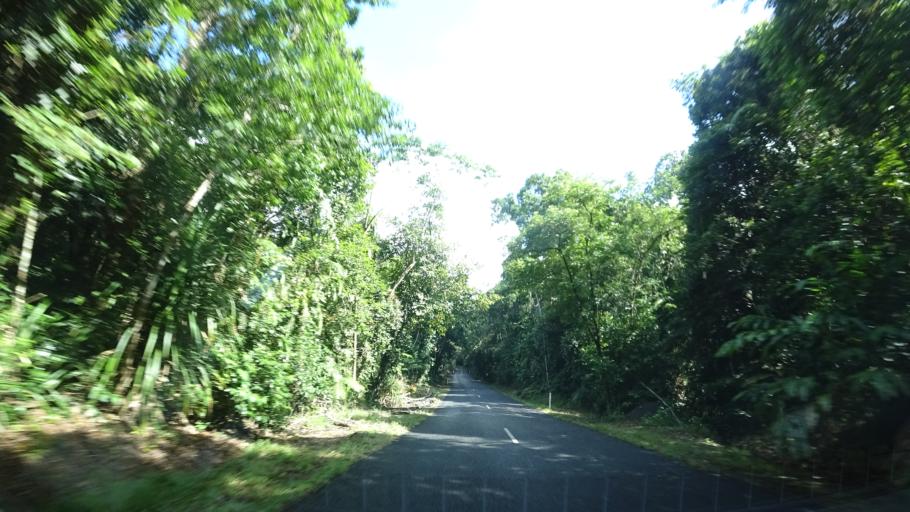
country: AU
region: Queensland
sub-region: Cairns
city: Port Douglas
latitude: -16.1380
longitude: 145.4350
